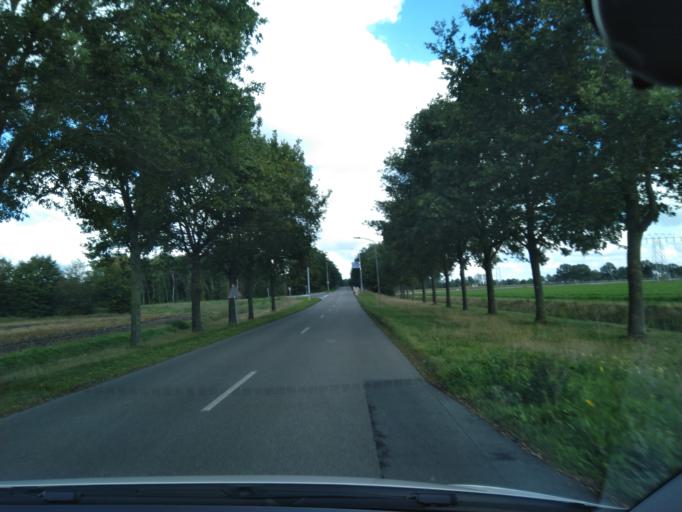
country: NL
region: Groningen
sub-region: Gemeente Veendam
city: Veendam
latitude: 53.0906
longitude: 6.9093
